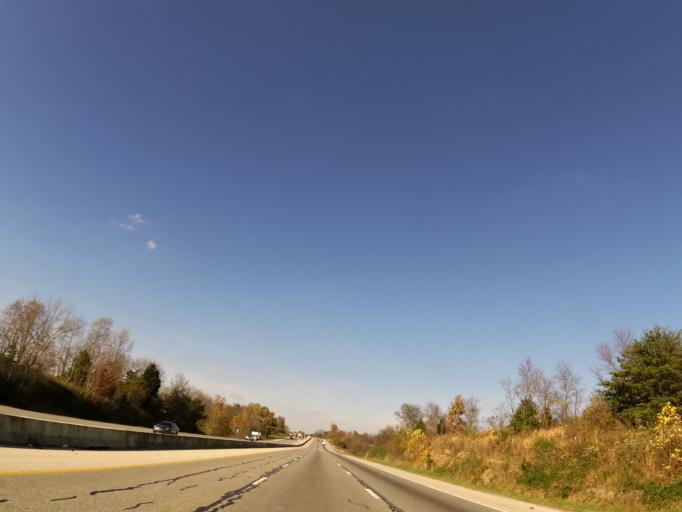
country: US
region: Kentucky
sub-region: Laurel County
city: London
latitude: 37.0531
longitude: -84.0983
